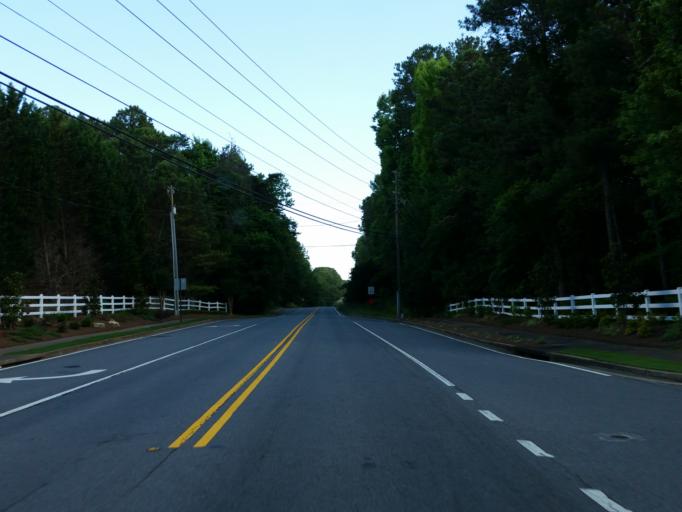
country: US
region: Georgia
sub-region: Cherokee County
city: Woodstock
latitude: 34.0537
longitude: -84.4850
